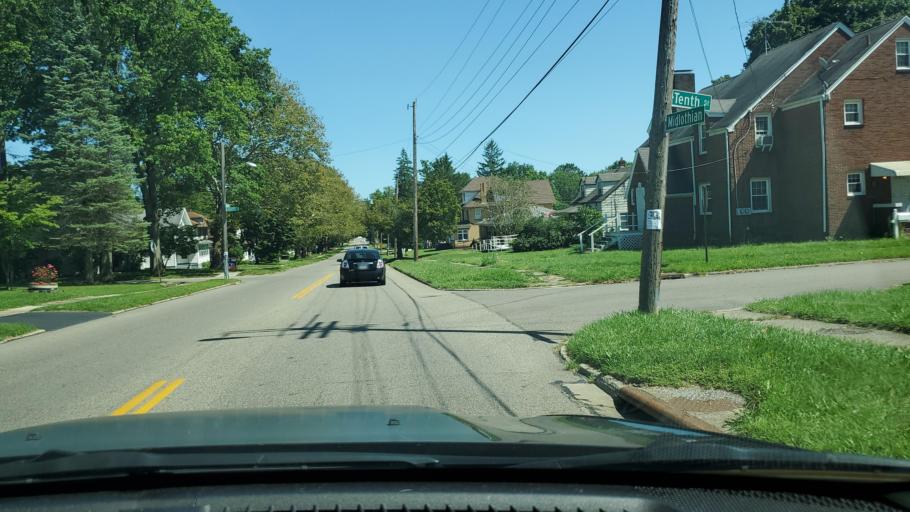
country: US
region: Ohio
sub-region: Mahoning County
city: Struthers
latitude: 41.0606
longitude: -80.6117
